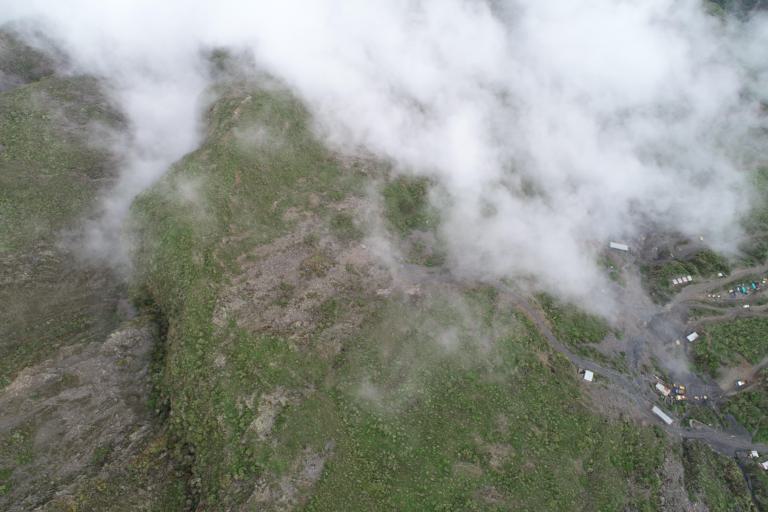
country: BO
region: La Paz
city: Sorata
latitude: -15.5211
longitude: -68.6648
